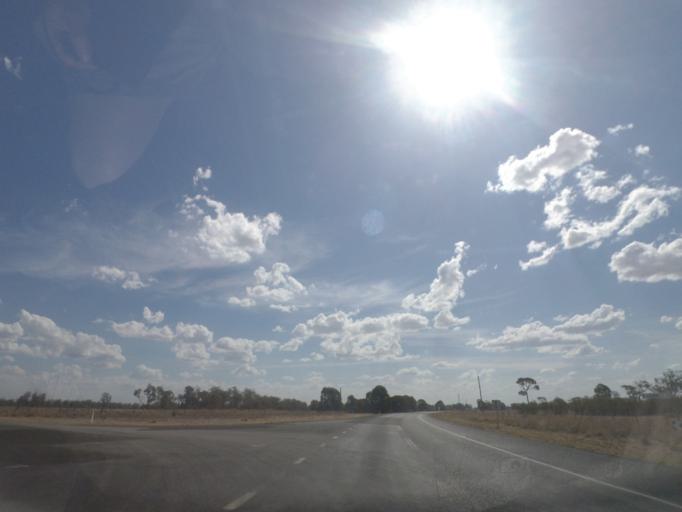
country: AU
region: Queensland
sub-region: Southern Downs
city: Stanthorpe
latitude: -28.4138
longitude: 151.1636
